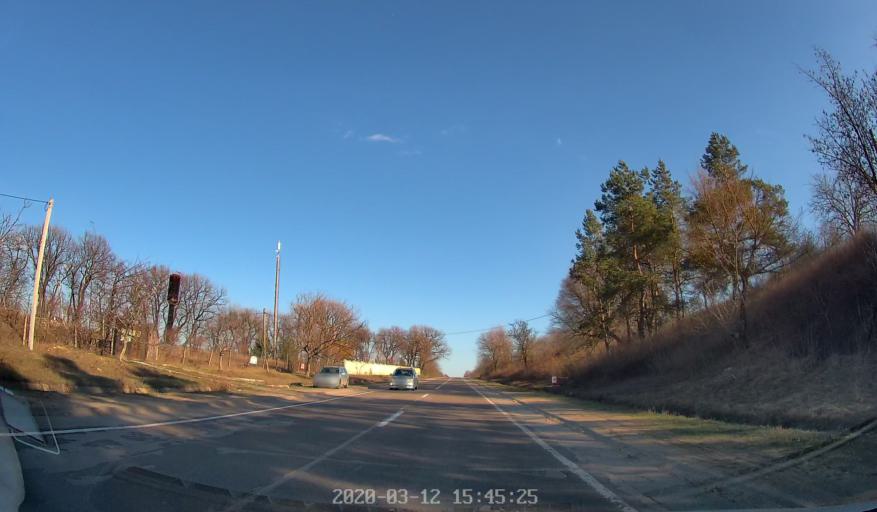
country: MD
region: Chisinau
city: Stauceni
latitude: 47.1060
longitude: 28.8750
